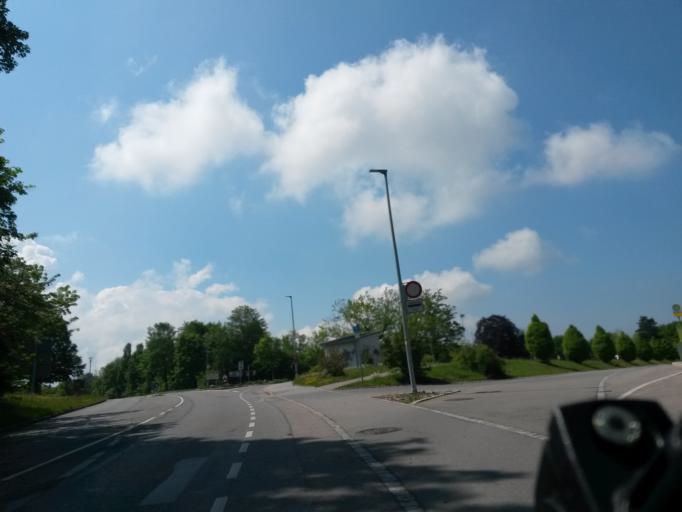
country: DE
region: Baden-Wuerttemberg
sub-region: Tuebingen Region
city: Bad Waldsee
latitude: 47.9150
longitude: 9.7569
